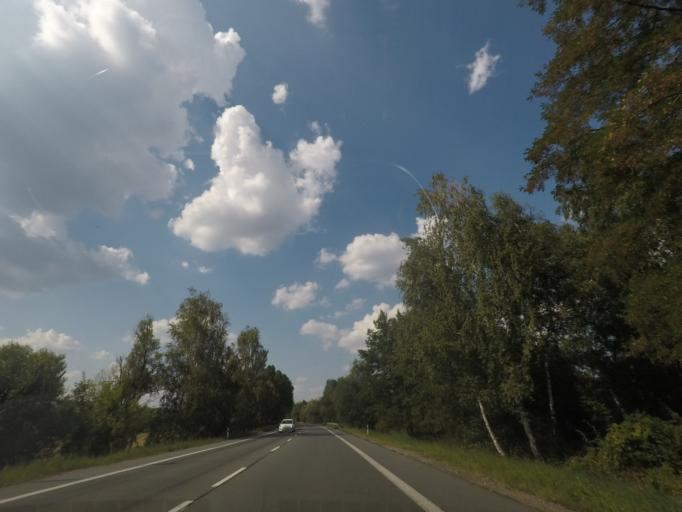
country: CZ
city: Tyniste nad Orlici
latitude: 50.1506
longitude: 16.0691
